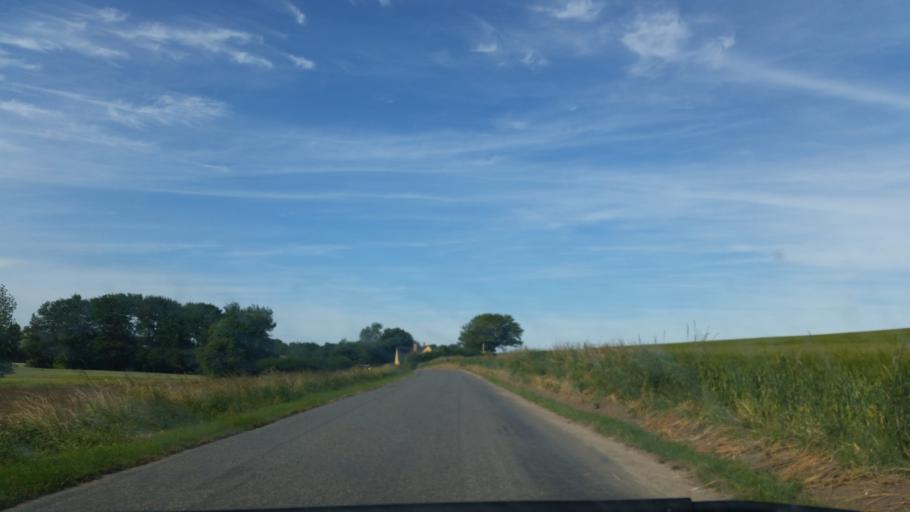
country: DK
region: Central Jutland
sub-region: Samso Kommune
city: Tranebjerg
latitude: 55.8362
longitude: 10.5630
